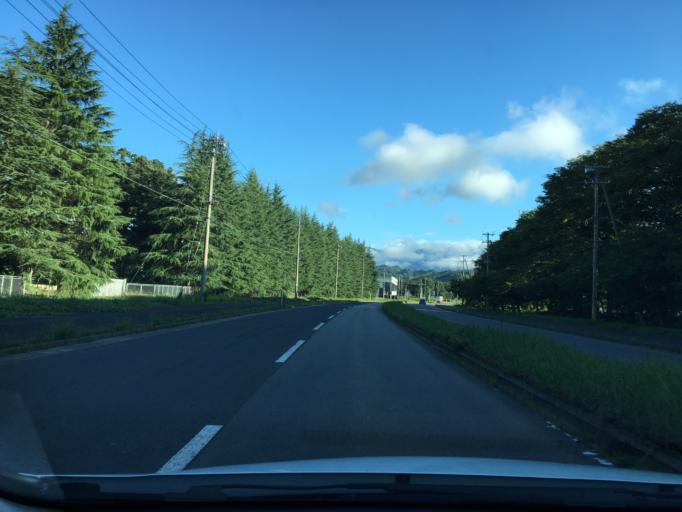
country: JP
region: Yamagata
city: Yonezawa
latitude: 37.9059
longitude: 140.1665
